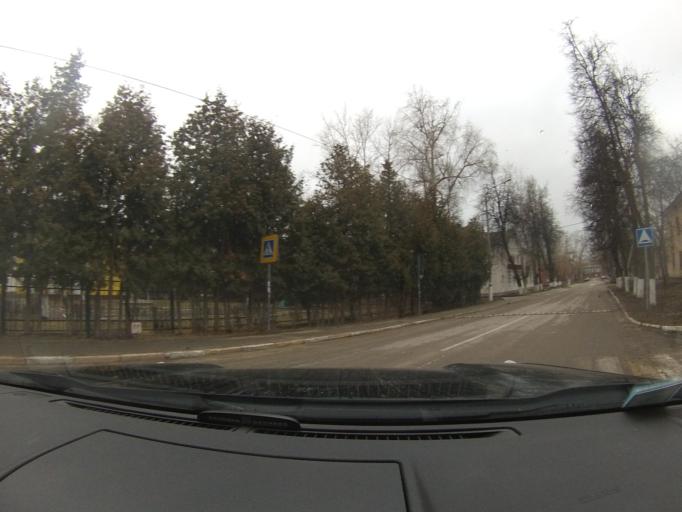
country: RU
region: Moskovskaya
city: Peski
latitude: 55.2472
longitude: 38.7627
